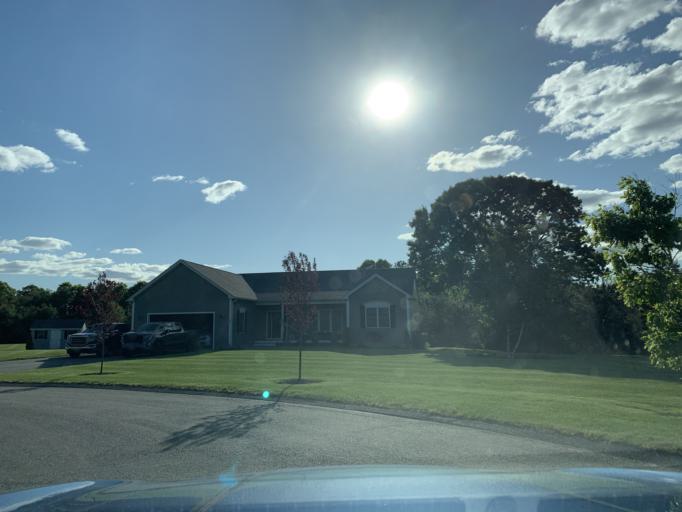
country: US
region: Rhode Island
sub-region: Kent County
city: East Greenwich
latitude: 41.6331
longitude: -71.4633
